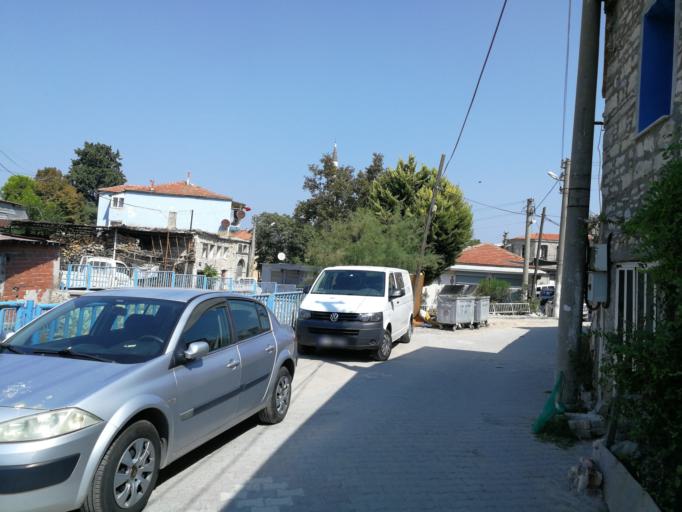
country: TR
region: Izmir
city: Urla
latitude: 38.3212
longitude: 26.7670
